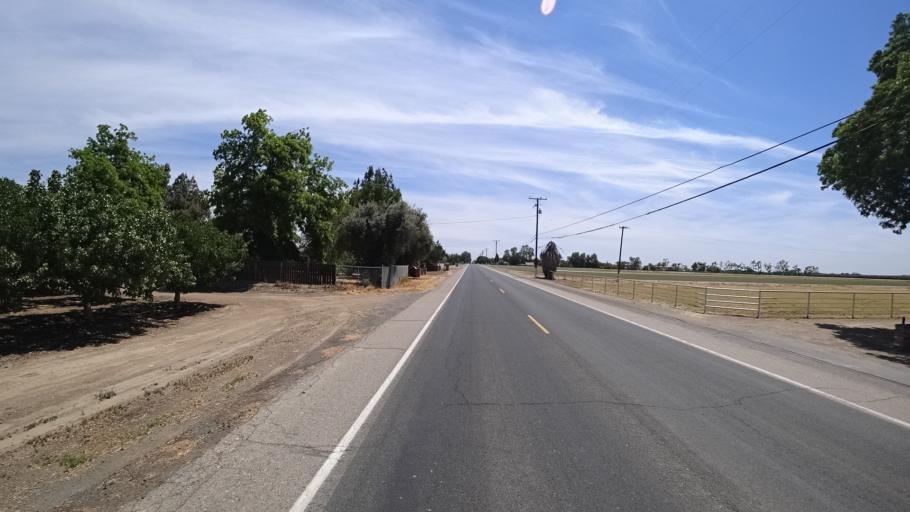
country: US
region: California
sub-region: Kings County
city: Armona
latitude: 36.3426
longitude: -119.7215
